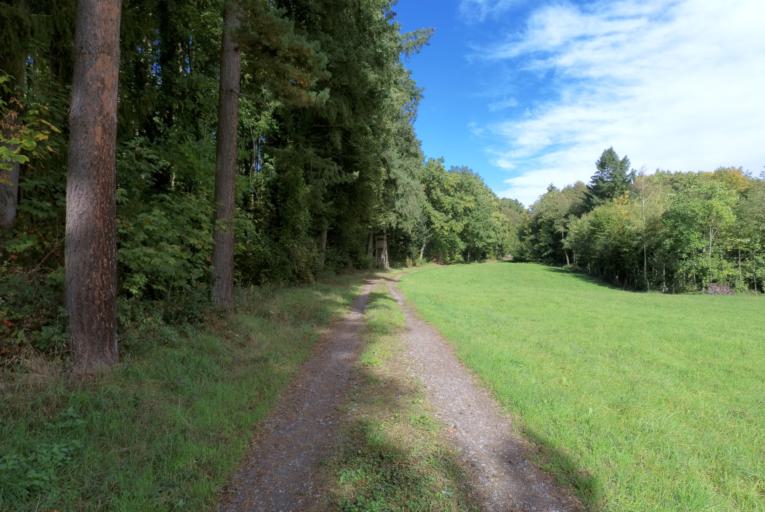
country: DE
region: Baden-Wuerttemberg
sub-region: Karlsruhe Region
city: Aglasterhausen
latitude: 49.3437
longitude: 8.9880
